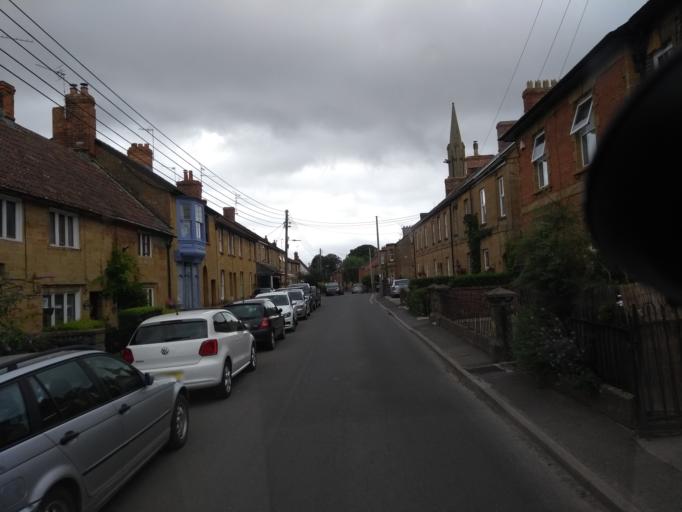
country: GB
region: England
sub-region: Somerset
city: Martock
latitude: 50.9747
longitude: -2.7671
